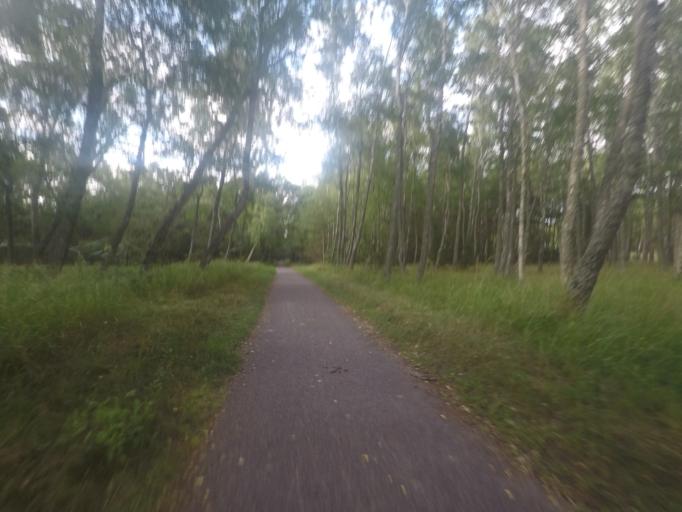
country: LT
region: Klaipedos apskritis
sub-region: Klaipeda
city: Klaipeda
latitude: 55.6490
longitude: 21.1080
